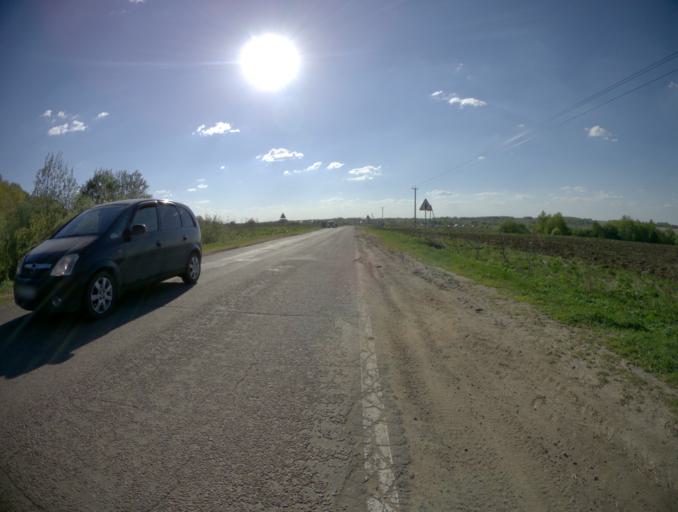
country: RU
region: Ivanovo
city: Gavrilov Posad
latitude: 56.3462
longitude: 40.1655
